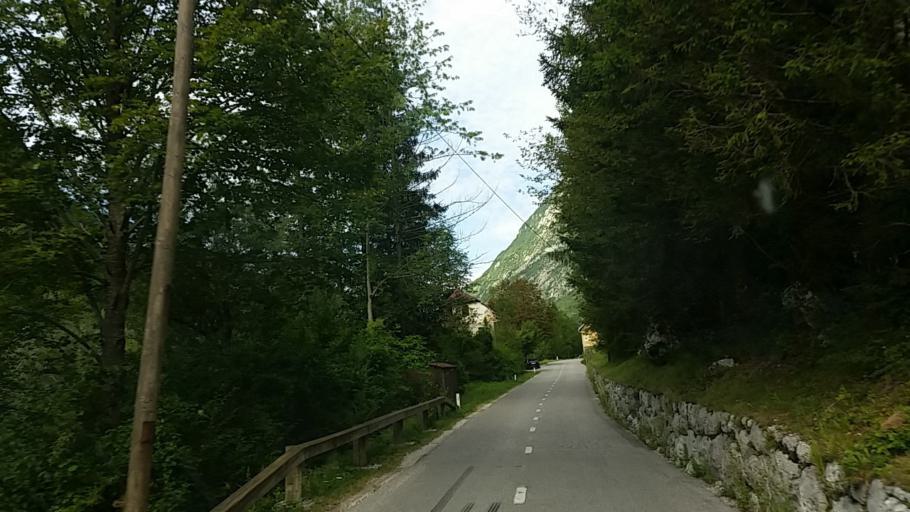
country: SI
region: Bovec
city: Bovec
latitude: 46.3418
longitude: 13.6750
